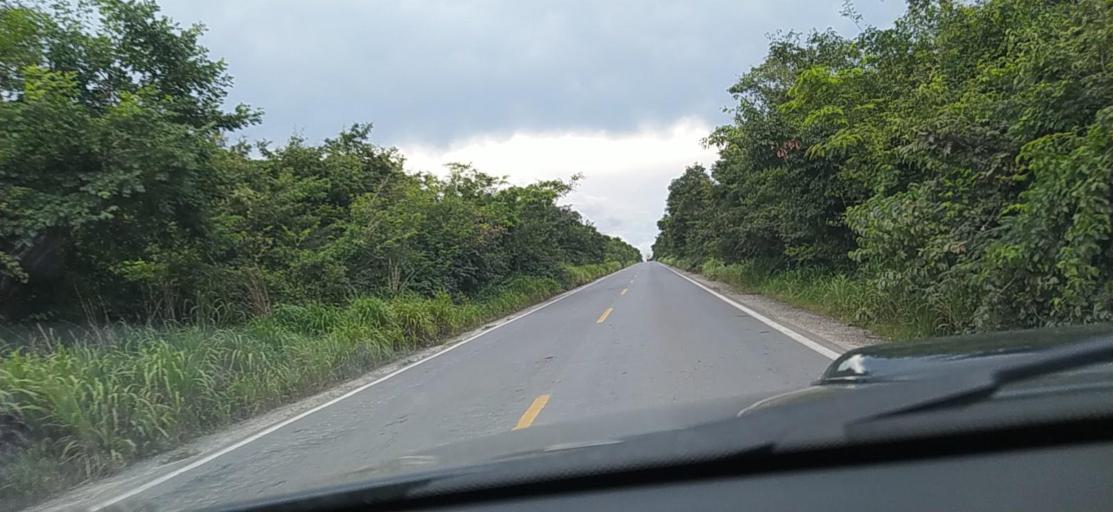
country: BR
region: Minas Gerais
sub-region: Francisco Sa
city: Francisco Sa
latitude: -16.2291
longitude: -43.6123
